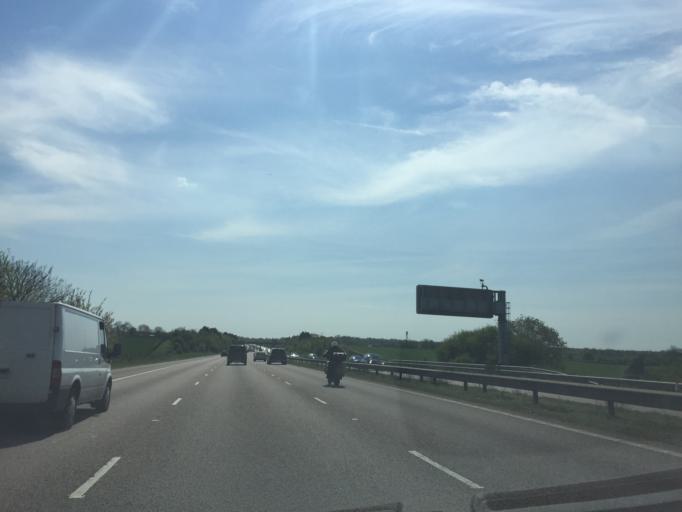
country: GB
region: England
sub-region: Essex
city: Epping
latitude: 51.7285
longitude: 0.1403
